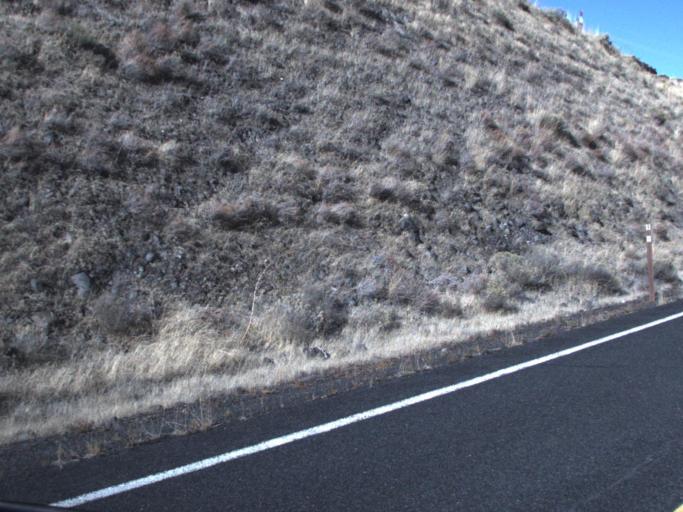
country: US
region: Washington
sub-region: Franklin County
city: Connell
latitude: 46.5391
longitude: -118.5631
